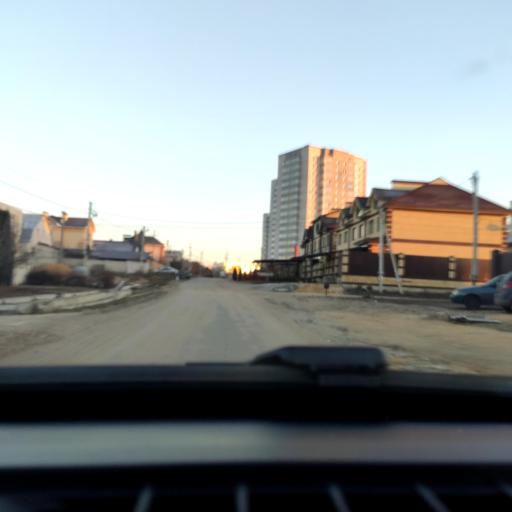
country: RU
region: Voronezj
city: Podgornoye
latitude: 51.7243
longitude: 39.1392
